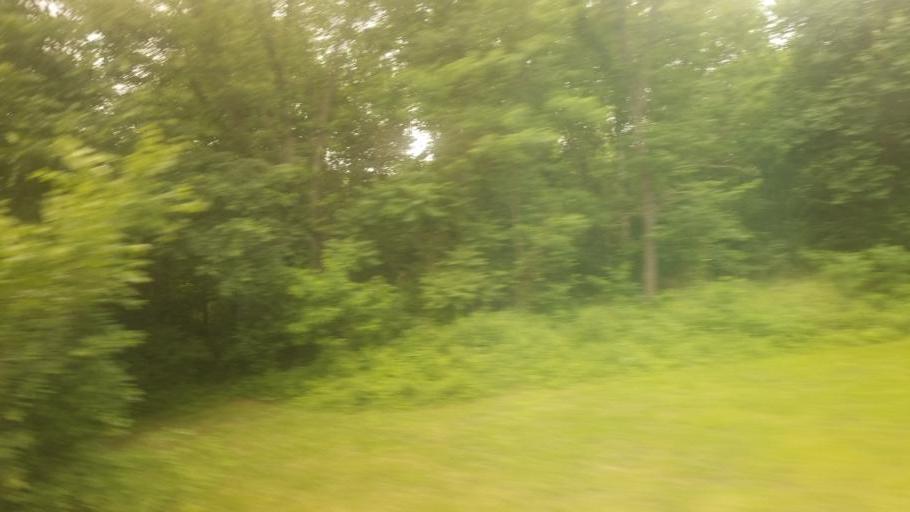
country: US
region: West Virginia
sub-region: Morgan County
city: Berkeley Springs
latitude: 39.6271
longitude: -78.3769
